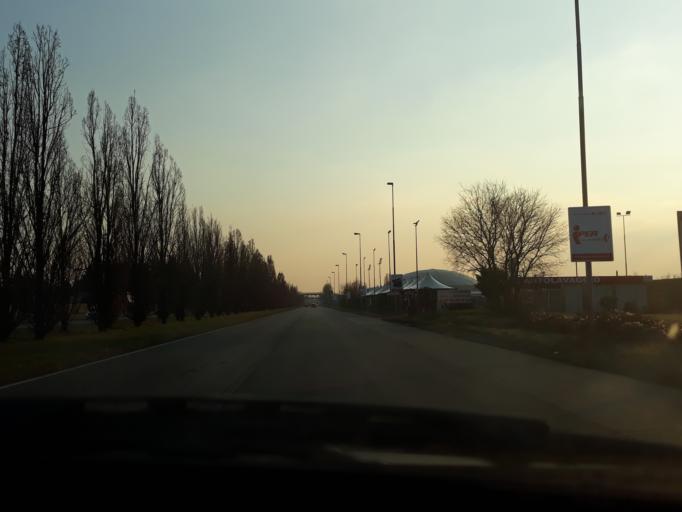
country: IT
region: Lombardy
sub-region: Provincia di Monza e Brianza
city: Villasanta
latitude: 45.5902
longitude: 9.3111
